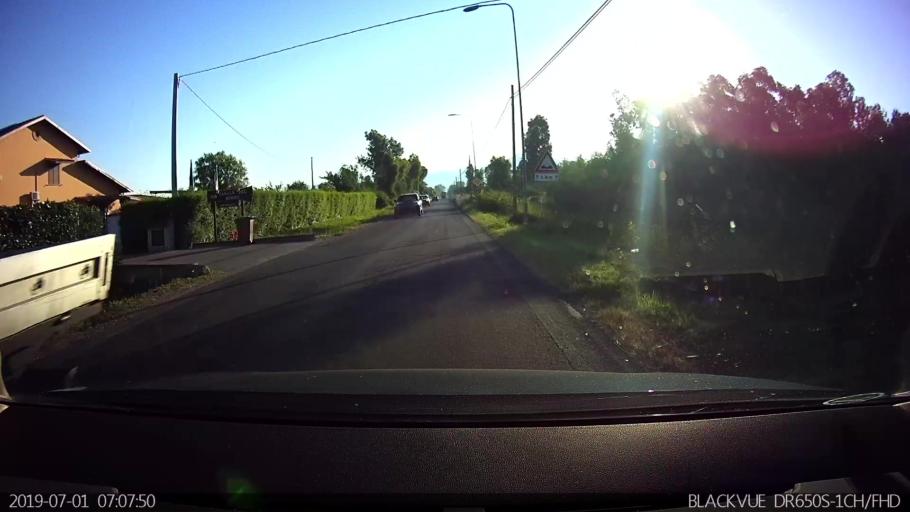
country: IT
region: Latium
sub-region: Provincia di Latina
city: Borgo Hermada
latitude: 41.2921
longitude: 13.1432
